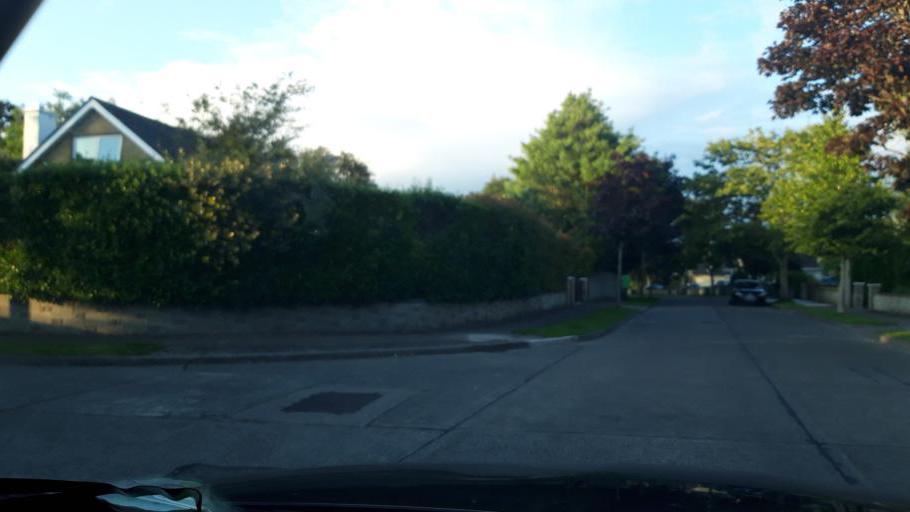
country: IE
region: Leinster
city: Malahide
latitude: 53.4484
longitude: -6.1715
